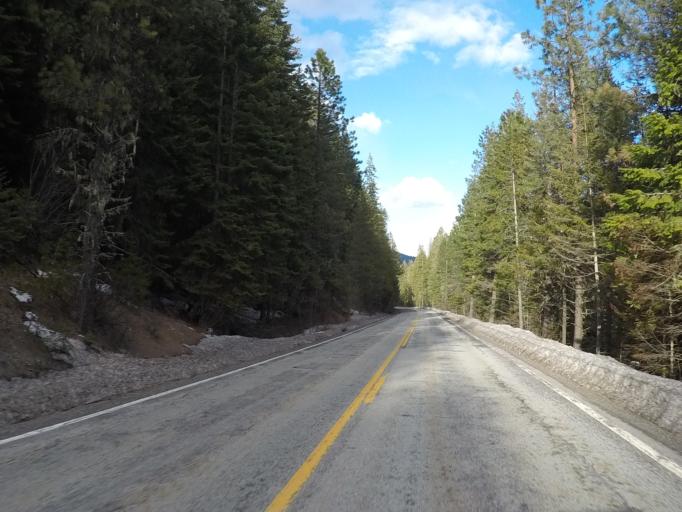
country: US
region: Montana
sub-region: Mineral County
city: Superior
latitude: 46.4930
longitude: -114.8684
